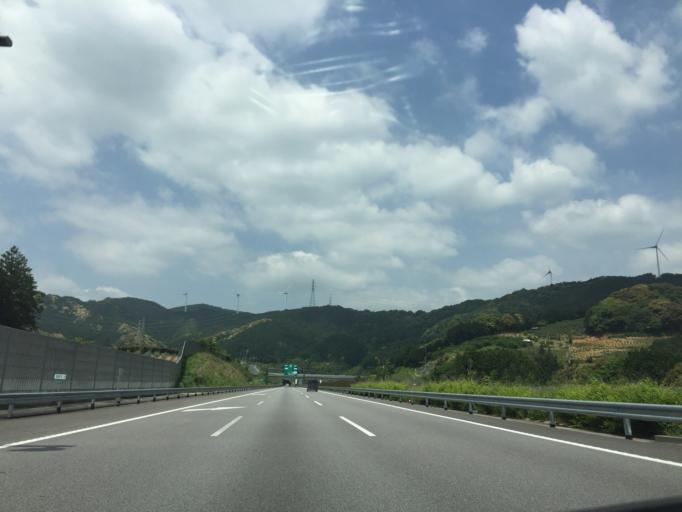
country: JP
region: Shizuoka
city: Hamakita
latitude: 34.8497
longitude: 137.7215
